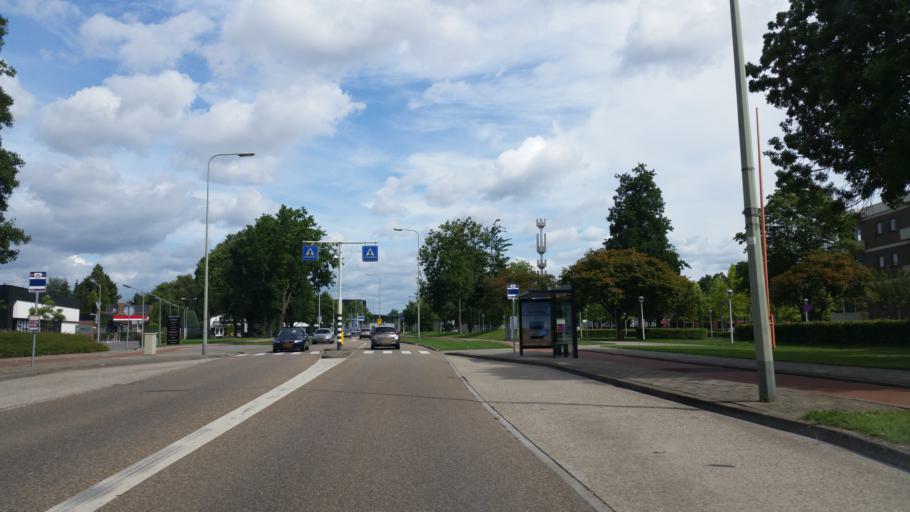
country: NL
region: Limburg
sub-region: Gemeente Maastricht
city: Heer
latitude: 50.8498
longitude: 5.7318
